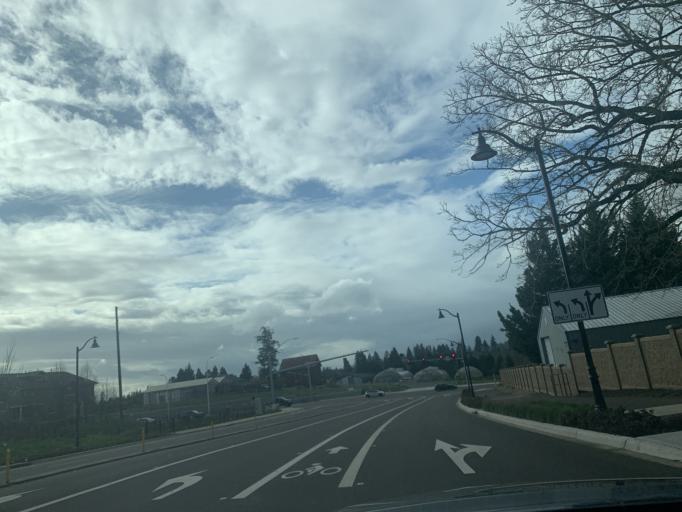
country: US
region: Oregon
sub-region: Washington County
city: Bethany
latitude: 45.5629
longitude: -122.8662
